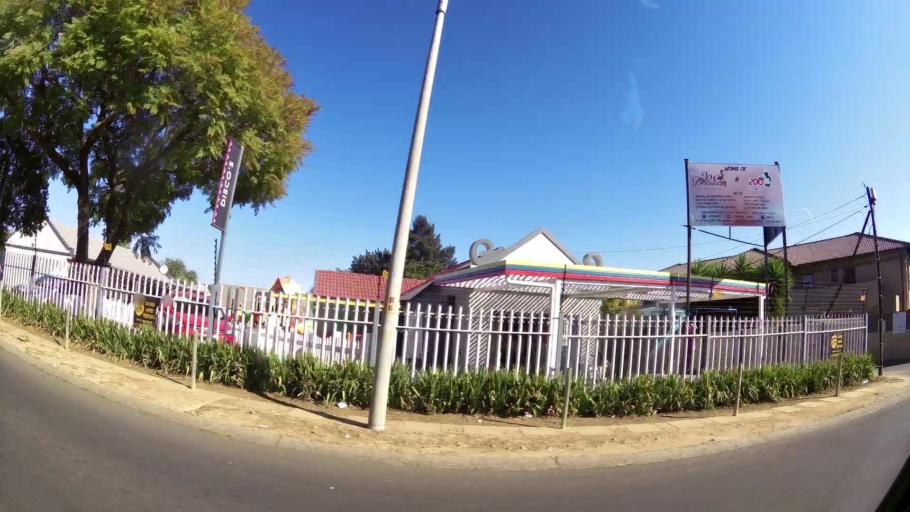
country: ZA
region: Gauteng
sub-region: Ekurhuleni Metropolitan Municipality
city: Germiston
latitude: -26.3074
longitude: 28.0951
